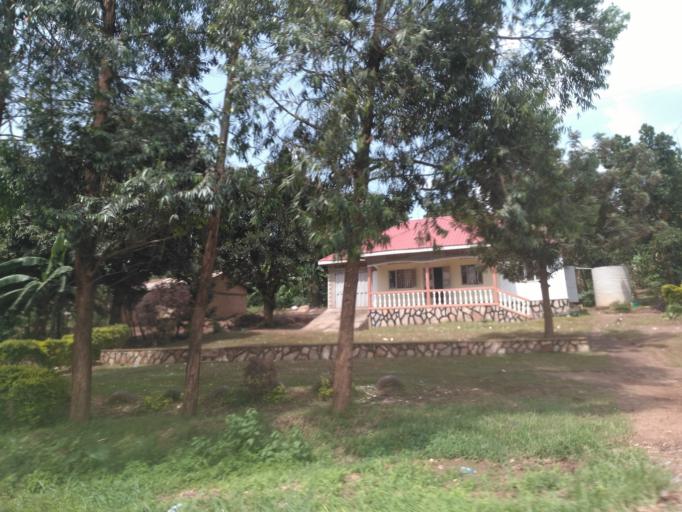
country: UG
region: Central Region
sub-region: Wakiso District
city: Bweyogerere
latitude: 0.4885
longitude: 32.6108
